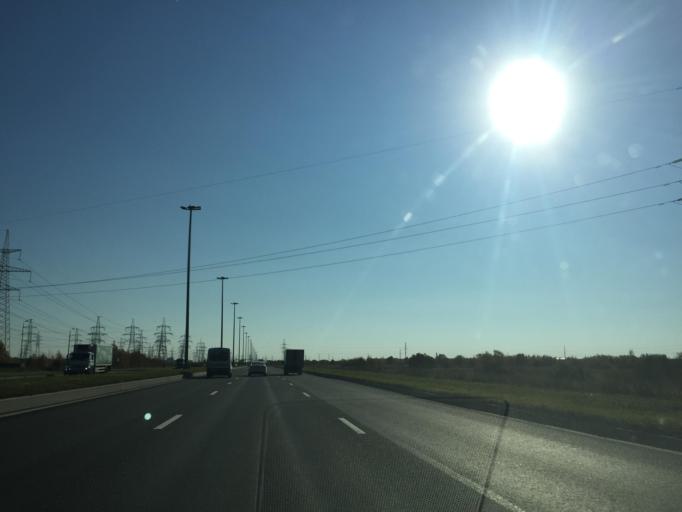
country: RU
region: St.-Petersburg
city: Petro-Slavyanka
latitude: 59.7586
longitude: 30.5147
